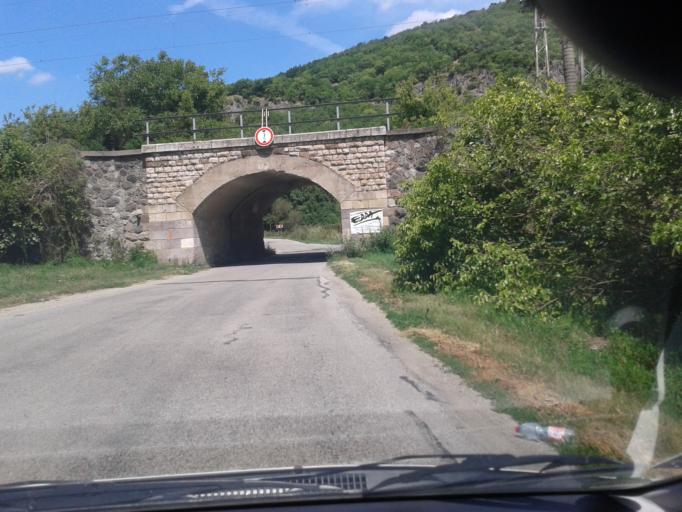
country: HU
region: Komarom-Esztergom
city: Esztergom
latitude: 47.8235
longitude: 18.7472
